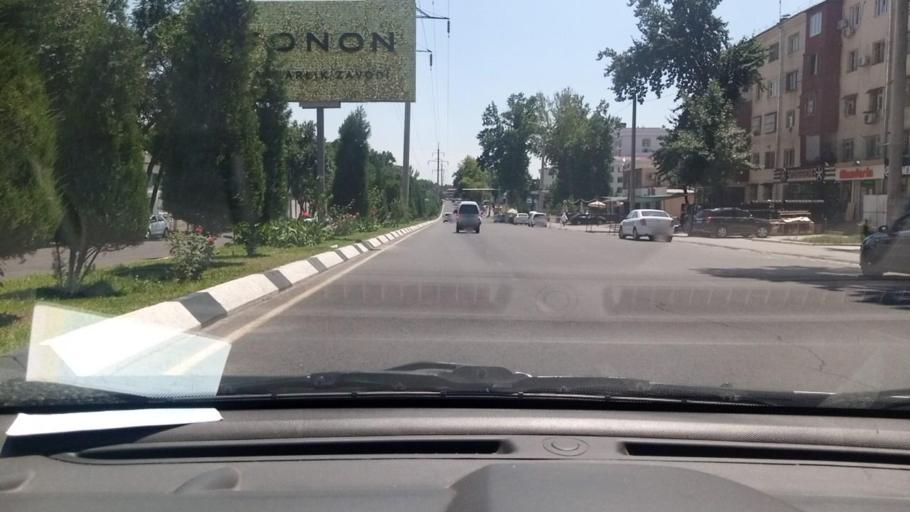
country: UZ
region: Toshkent Shahri
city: Tashkent
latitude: 41.2888
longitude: 69.1943
